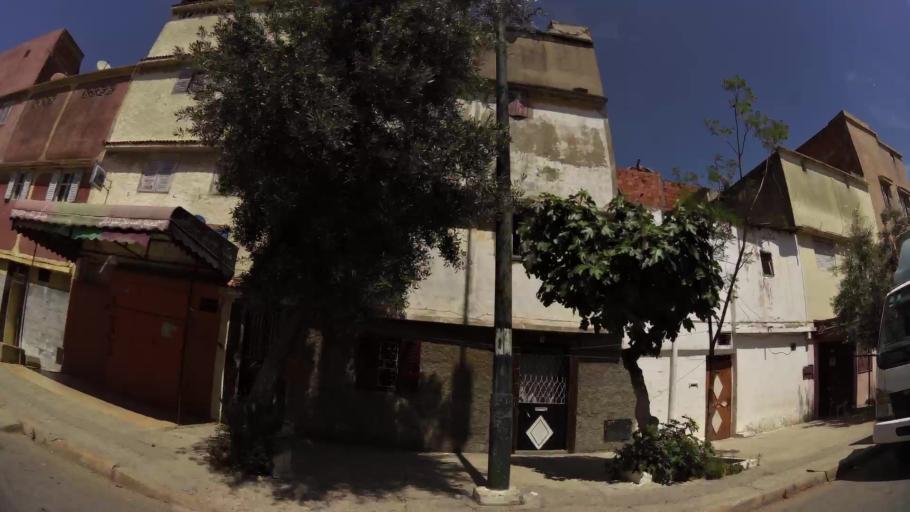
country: MA
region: Gharb-Chrarda-Beni Hssen
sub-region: Kenitra Province
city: Kenitra
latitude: 34.2509
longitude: -6.5461
